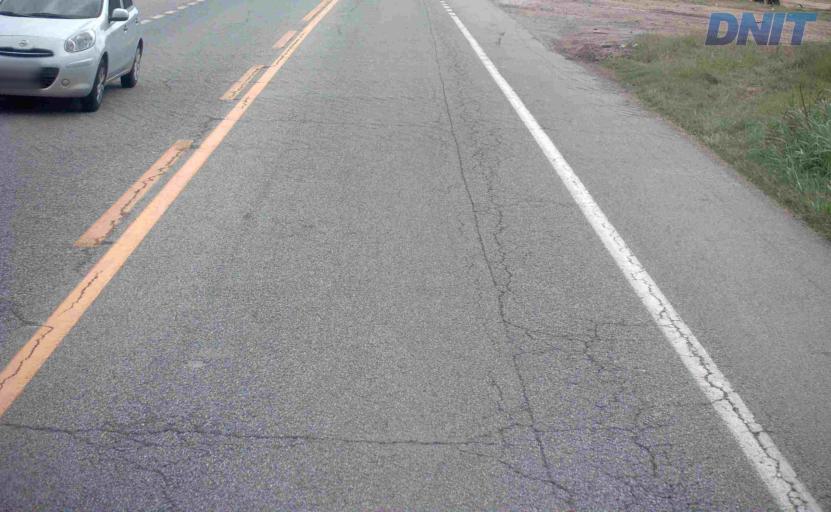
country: BR
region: Minas Gerais
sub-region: Caete
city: Caete
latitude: -19.7417
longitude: -43.5545
